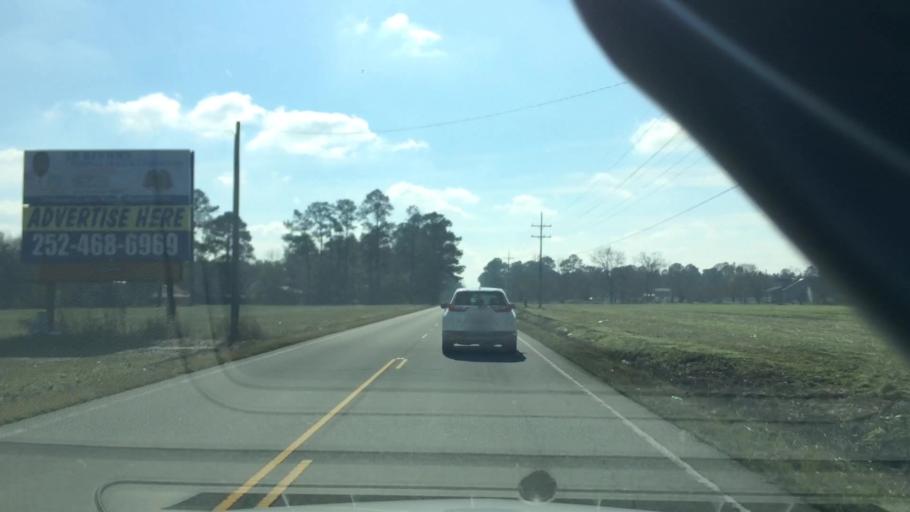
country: US
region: North Carolina
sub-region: Duplin County
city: Beulaville
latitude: 34.9029
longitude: -77.7796
